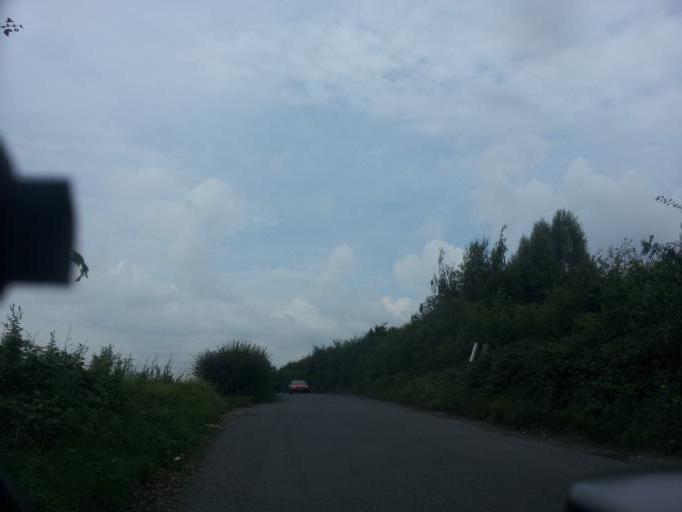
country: GB
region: England
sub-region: Kent
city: Sittingbourne
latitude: 51.3601
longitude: 0.7155
